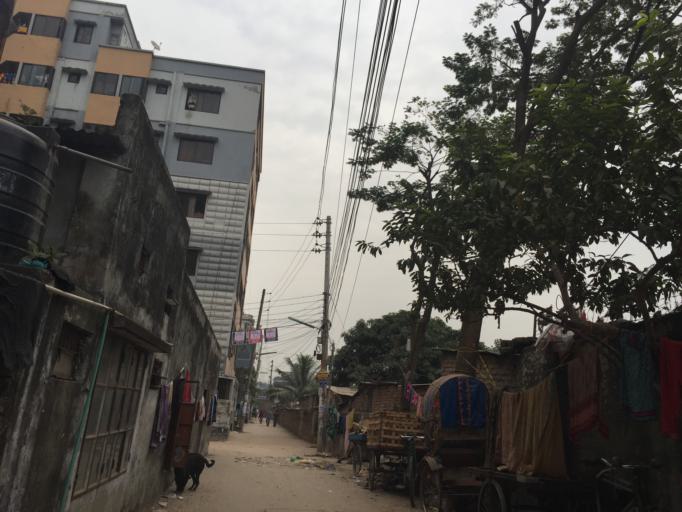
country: BD
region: Dhaka
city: Azimpur
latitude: 23.7887
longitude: 90.3558
